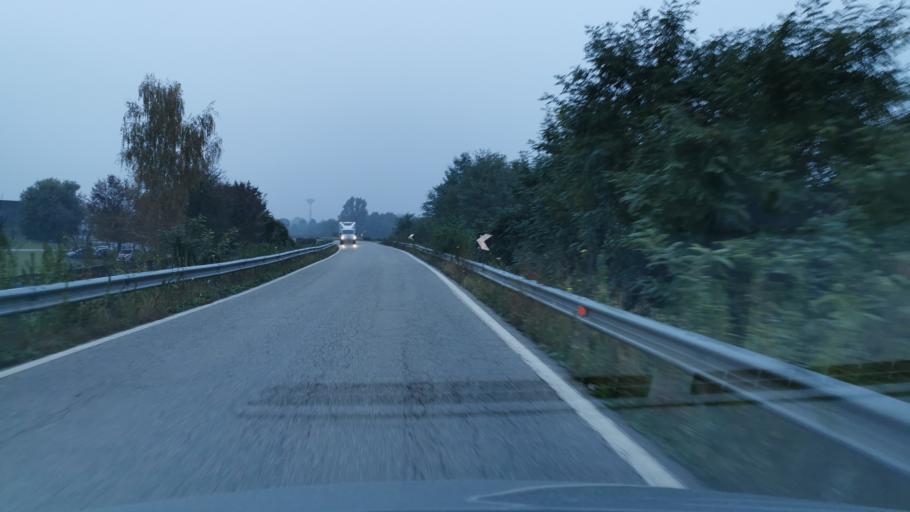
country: IT
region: Piedmont
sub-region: Provincia di Torino
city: Lusiglie
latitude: 45.3120
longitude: 7.7573
